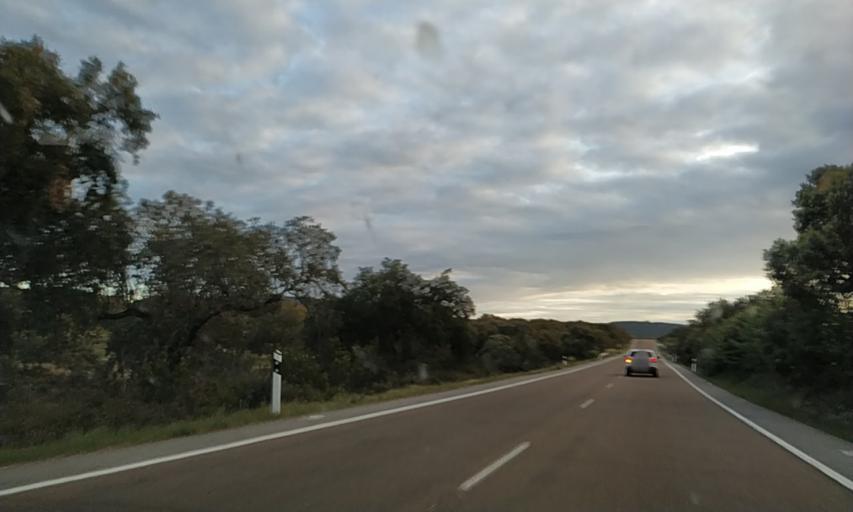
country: ES
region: Extremadura
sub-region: Provincia de Badajoz
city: Puebla de Obando
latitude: 39.2235
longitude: -6.5750
